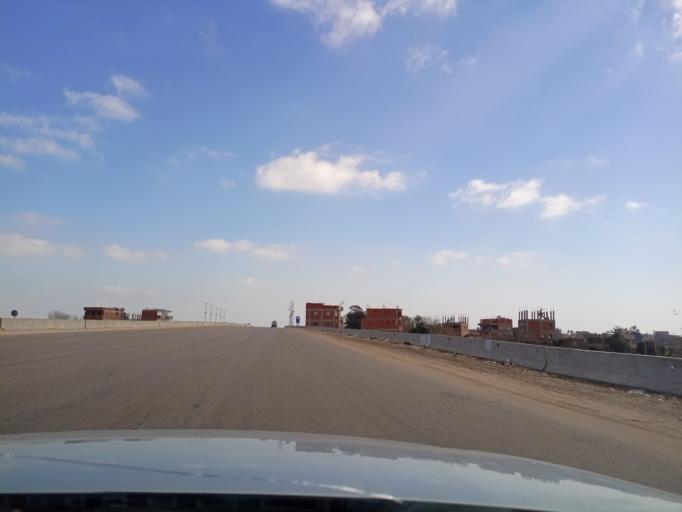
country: EG
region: Muhafazat al Minufiyah
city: Al Bajur
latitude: 30.4042
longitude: 31.0371
